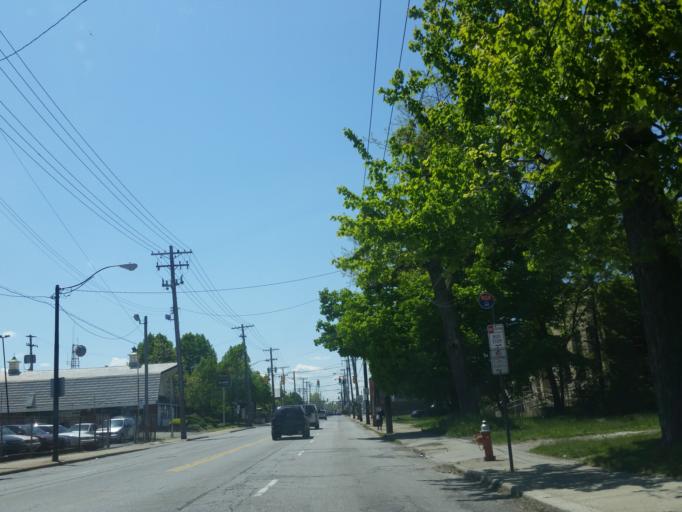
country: US
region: Ohio
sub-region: Cuyahoga County
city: East Cleveland
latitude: 41.5565
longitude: -81.5756
